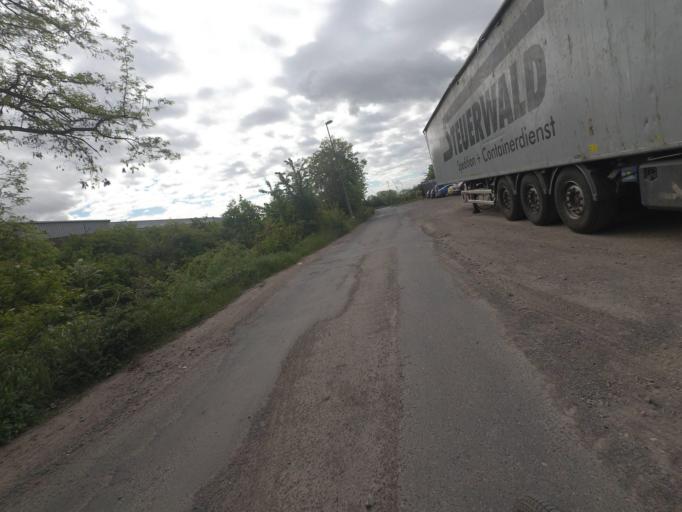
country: DE
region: Rheinland-Pfalz
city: Kirchheimbolanden
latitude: 49.6728
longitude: 8.0116
